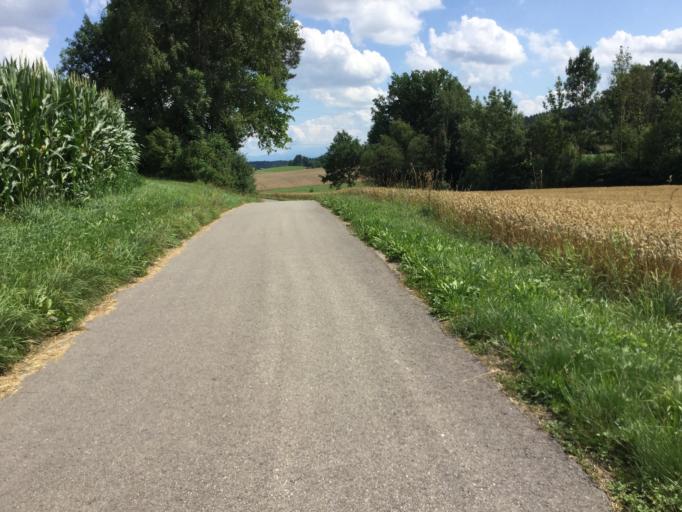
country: CH
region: Zurich
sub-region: Bezirk Pfaeffikon
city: Illnau / Unter-Illnau
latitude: 47.3954
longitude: 8.7293
